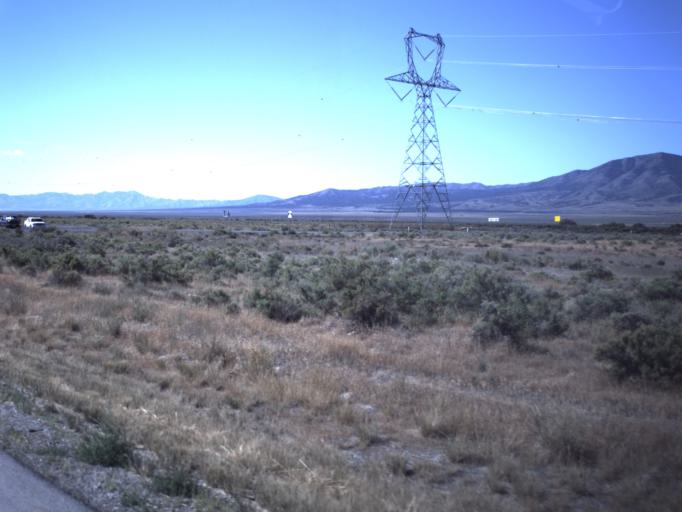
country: US
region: Utah
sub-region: Tooele County
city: Tooele
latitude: 40.3382
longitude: -112.4098
